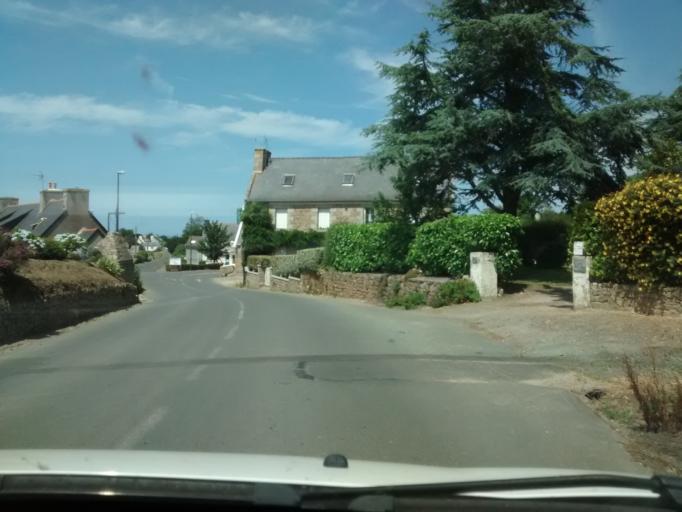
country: FR
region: Brittany
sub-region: Departement des Cotes-d'Armor
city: Trevou-Treguignec
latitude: 48.8131
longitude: -3.3355
